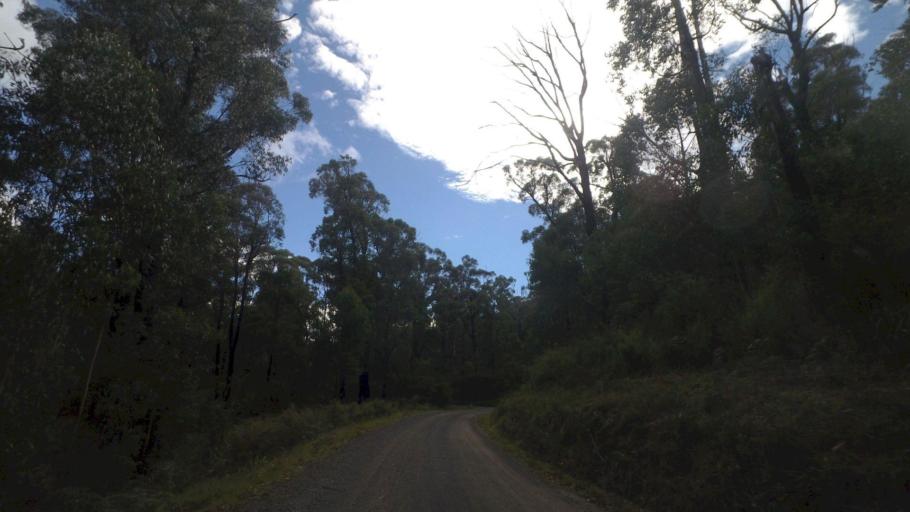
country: AU
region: Victoria
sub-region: Cardinia
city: Bunyip
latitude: -37.9919
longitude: 145.8148
